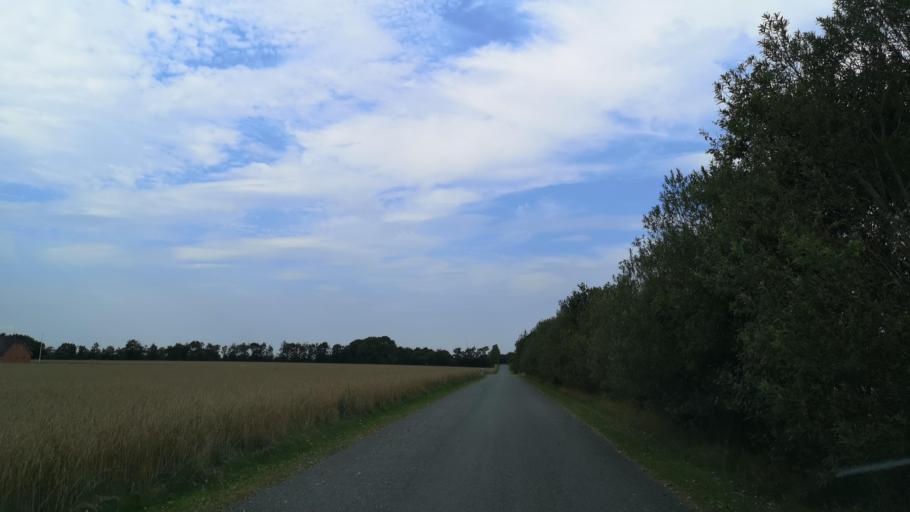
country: DK
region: Central Jutland
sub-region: Ringkobing-Skjern Kommune
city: Videbaek
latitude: 56.0722
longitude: 8.6808
